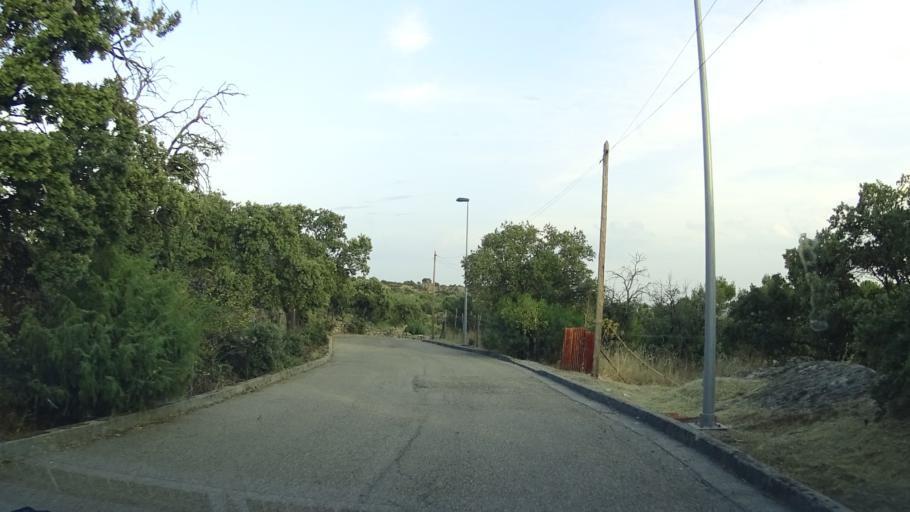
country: ES
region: Madrid
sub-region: Provincia de Madrid
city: Torrelodones
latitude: 40.5884
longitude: -3.9433
